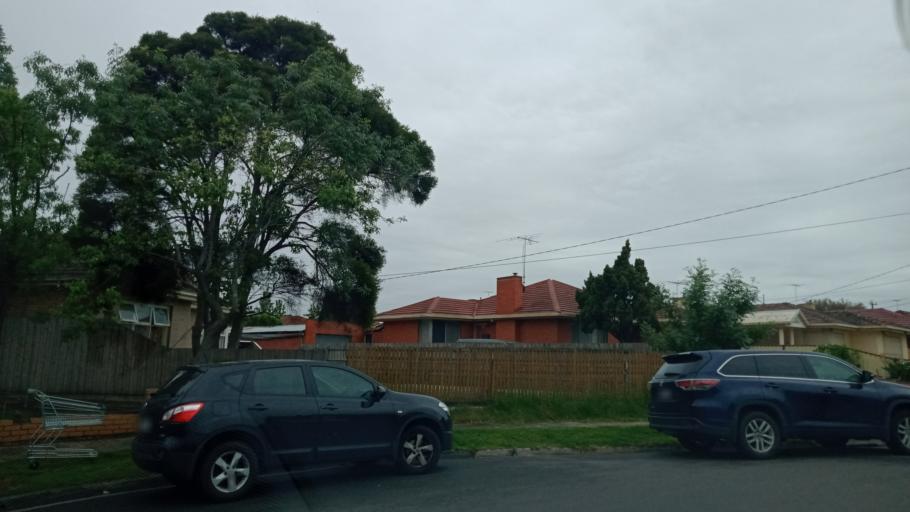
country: AU
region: Victoria
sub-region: Greater Dandenong
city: Springvale
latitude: -37.9431
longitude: 145.1628
